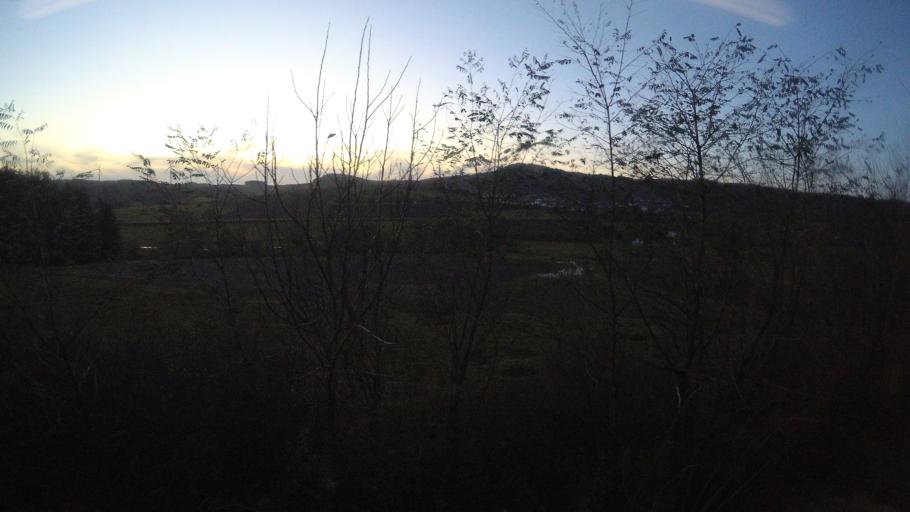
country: DE
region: Rheinland-Pfalz
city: Reichweiler
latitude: 49.5207
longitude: 7.2757
